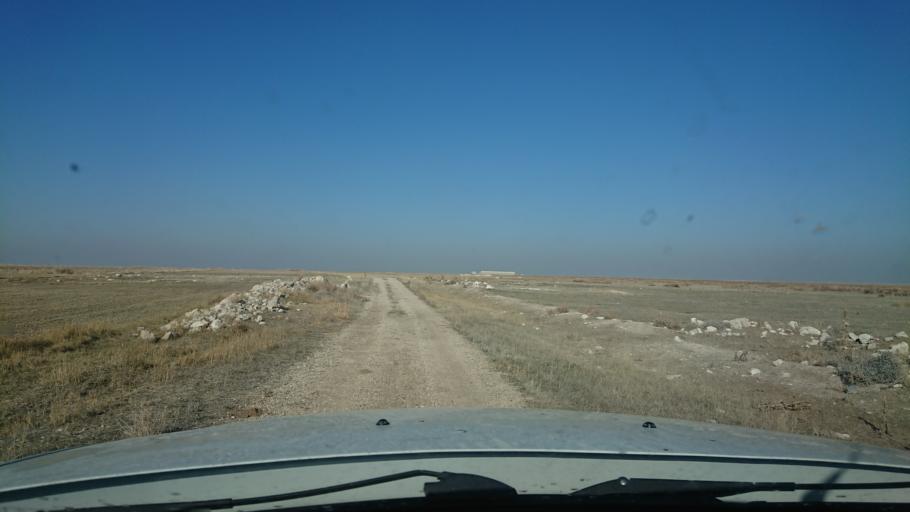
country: TR
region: Aksaray
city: Sultanhani
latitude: 38.3147
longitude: 33.5276
